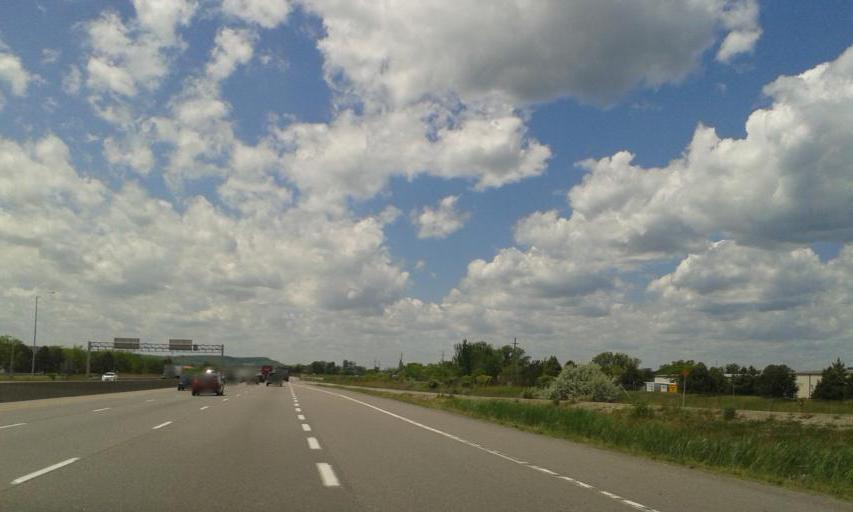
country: CA
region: Ontario
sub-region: Regional Municipality of Niagara
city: St. Catharines
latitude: 43.1892
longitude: -79.4788
